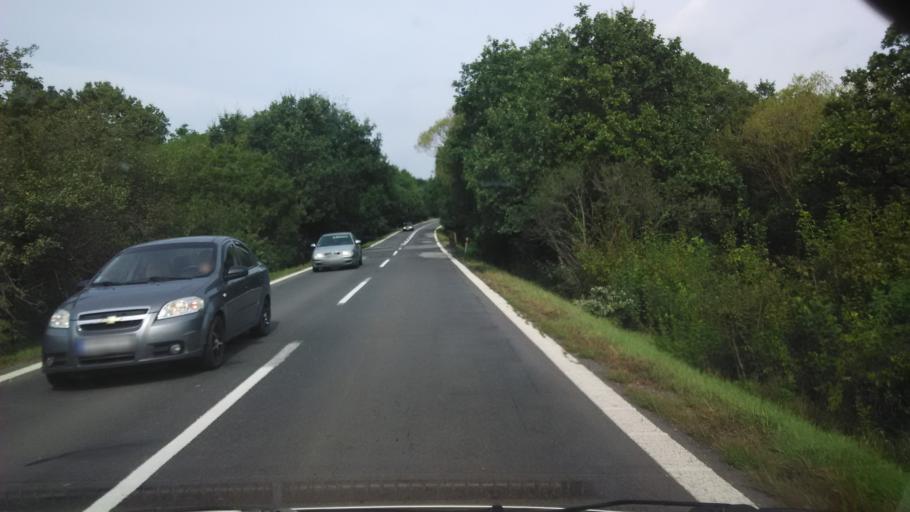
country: SK
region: Banskobystricky
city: Krupina
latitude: 48.2962
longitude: 19.0210
